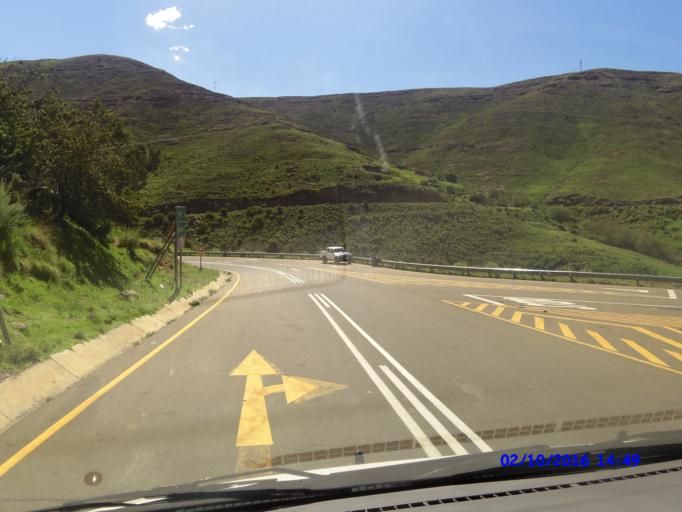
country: LS
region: Maseru
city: Nako
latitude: -29.4933
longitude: 28.0597
